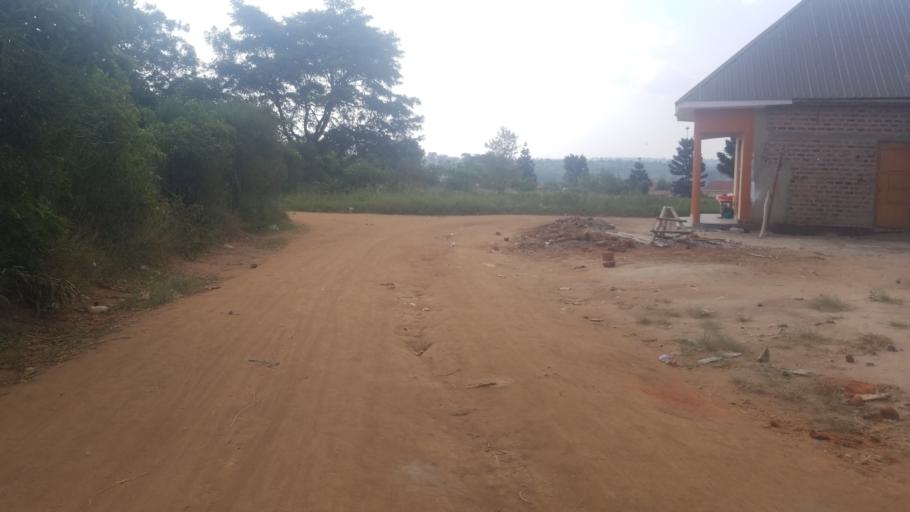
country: UG
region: Central Region
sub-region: Sembabule District
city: Sembabule
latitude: -0.0826
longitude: 31.4578
